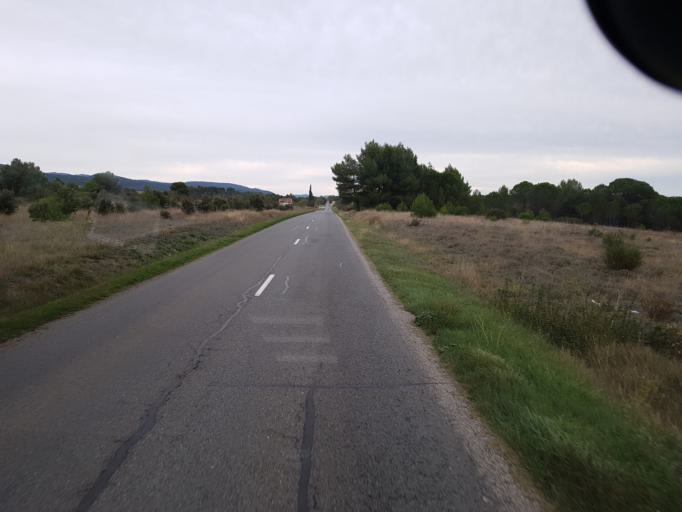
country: FR
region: Languedoc-Roussillon
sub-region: Departement de l'Aude
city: Caunes-Minervois
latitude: 43.3064
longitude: 2.4817
